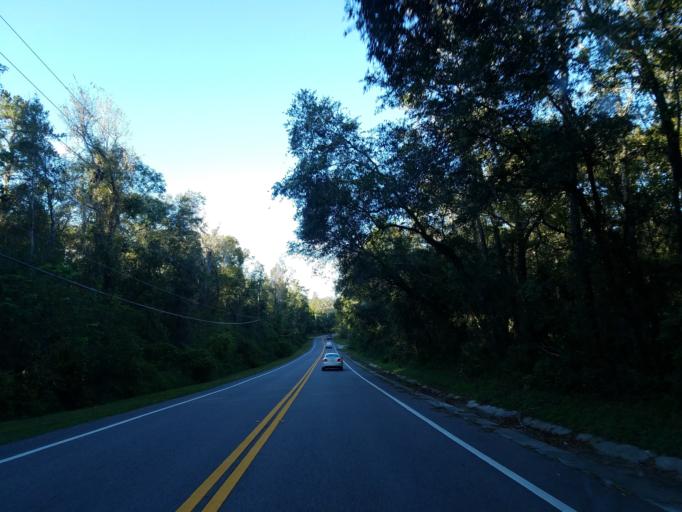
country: US
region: Florida
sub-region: Hernando County
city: Hill 'n Dale
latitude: 28.4746
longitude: -82.3025
